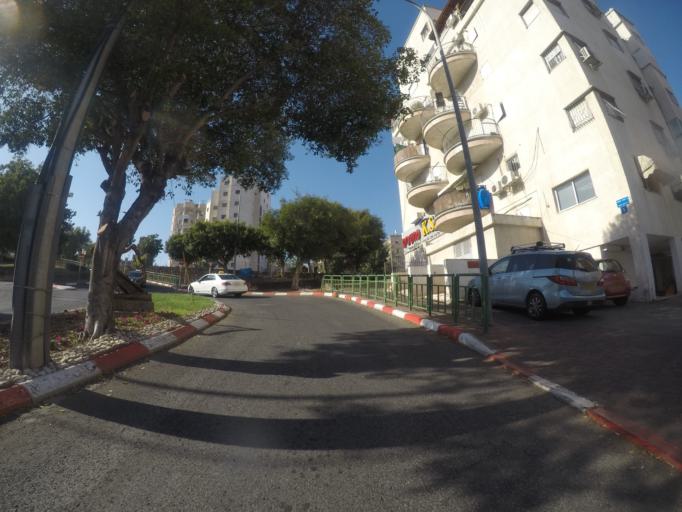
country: IL
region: Northern District
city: Tiberias
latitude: 32.7959
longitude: 35.5270
